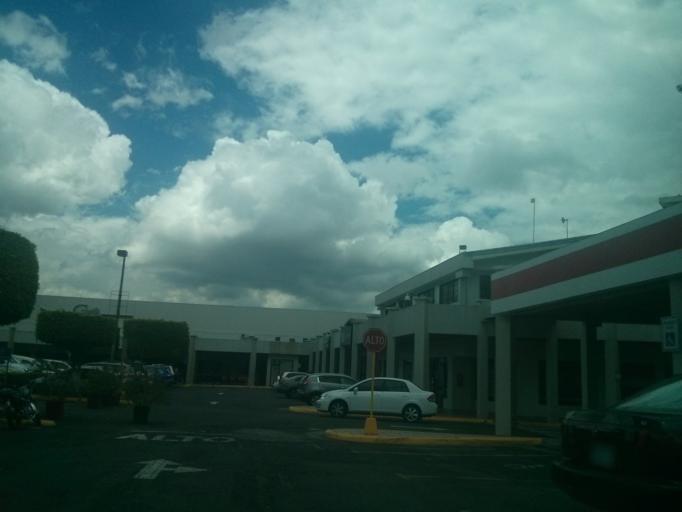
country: CR
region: San Jose
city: San Pedro
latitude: 9.9215
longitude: -84.0438
